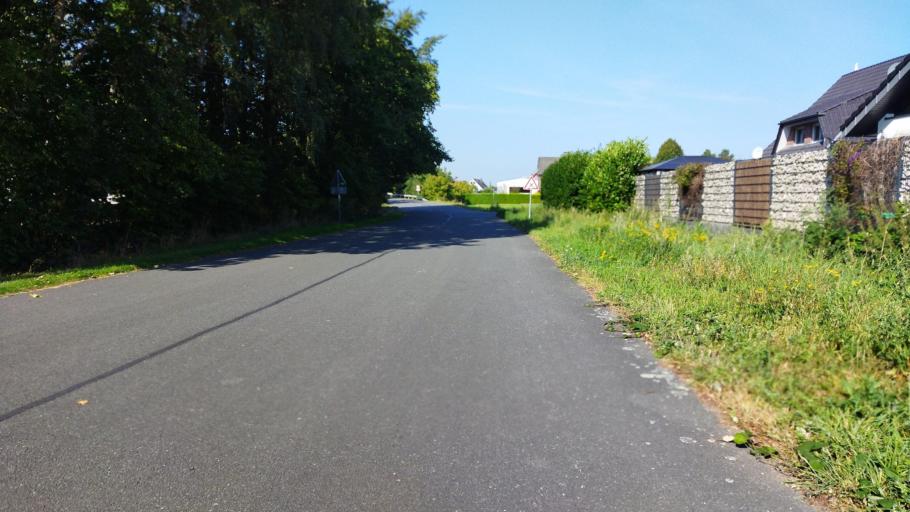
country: DE
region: North Rhine-Westphalia
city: Lengerich
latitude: 52.1658
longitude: 7.8951
